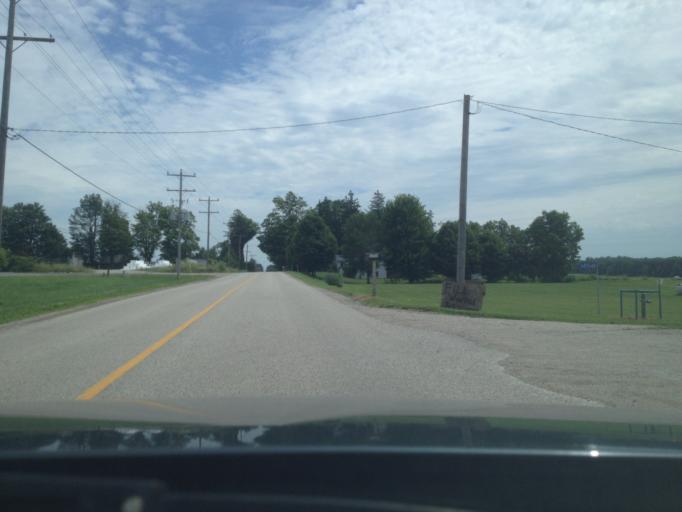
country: CA
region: Ontario
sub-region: Oxford County
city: Woodstock
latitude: 42.9983
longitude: -80.6250
